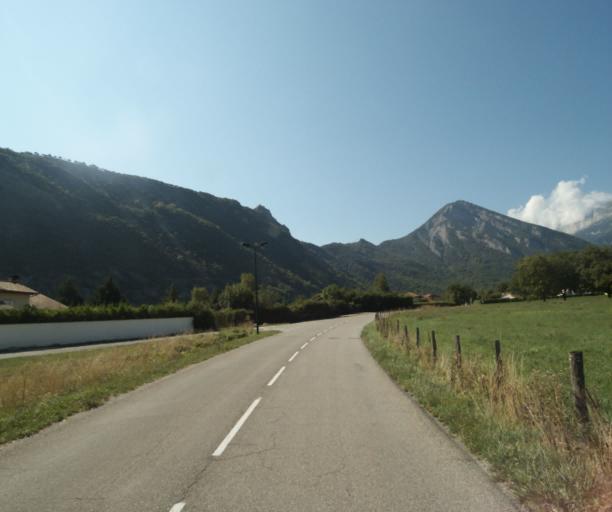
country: FR
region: Rhone-Alpes
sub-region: Departement de l'Isere
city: Saint-Paul-de-Varces
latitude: 45.0771
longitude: 5.6623
